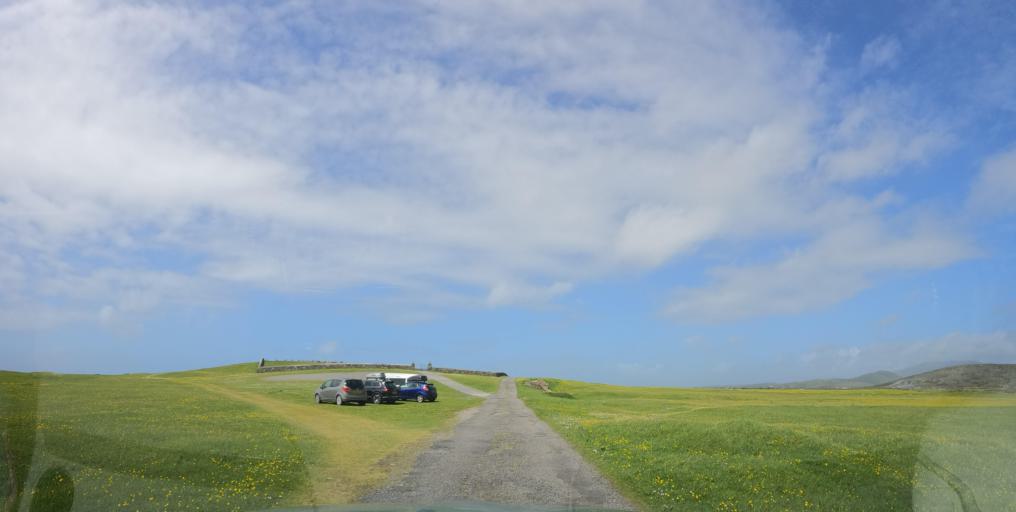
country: GB
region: Scotland
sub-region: Eilean Siar
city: Isle of South Uist
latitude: 57.1699
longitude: -7.4030
